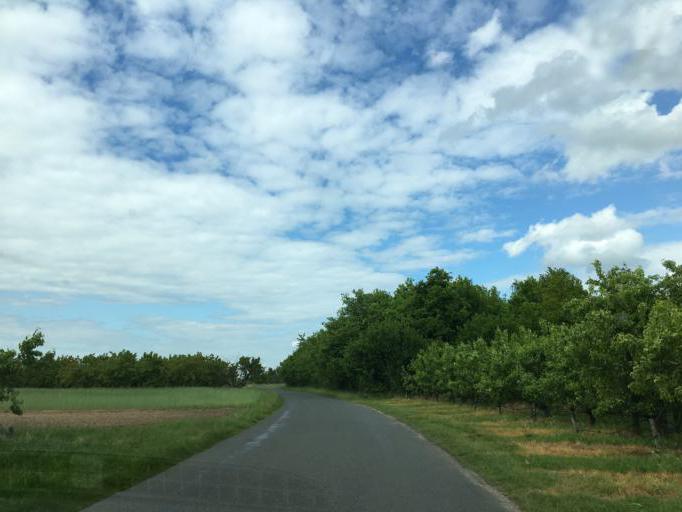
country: FR
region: Centre
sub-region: Departement du Loiret
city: Mareau-aux-Pres
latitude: 47.8354
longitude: 1.8035
